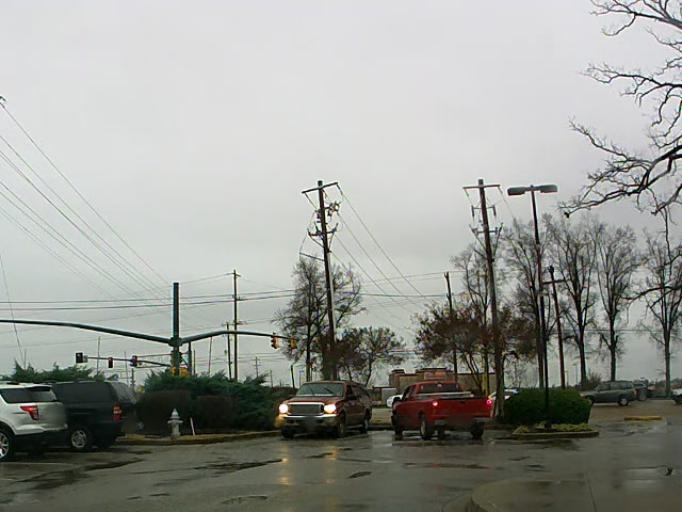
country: US
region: Tennessee
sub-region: Shelby County
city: Collierville
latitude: 35.0522
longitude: -89.7329
